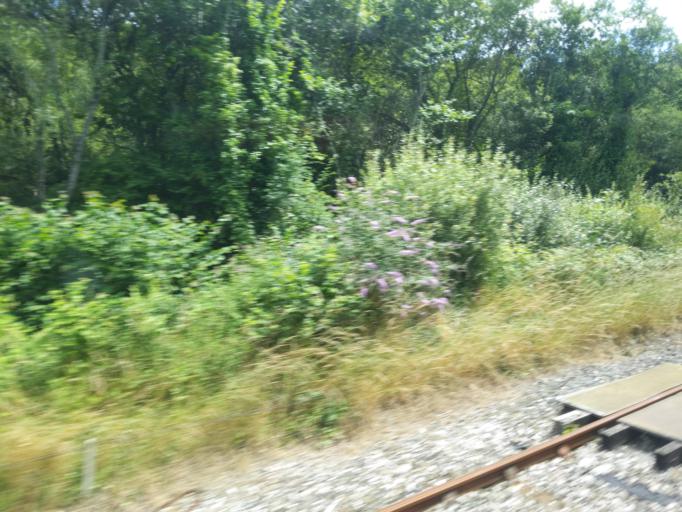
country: GB
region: England
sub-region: Cornwall
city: Par
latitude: 50.3581
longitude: -4.7038
